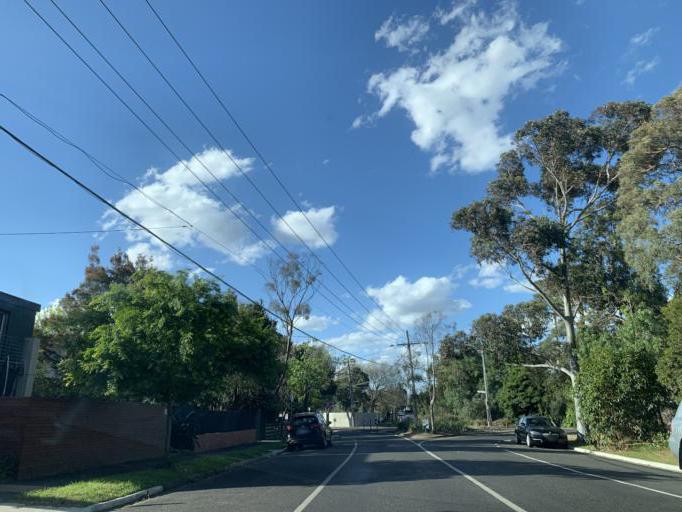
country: AU
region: Victoria
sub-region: Bayside
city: North Brighton
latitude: -37.9082
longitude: 145.0017
